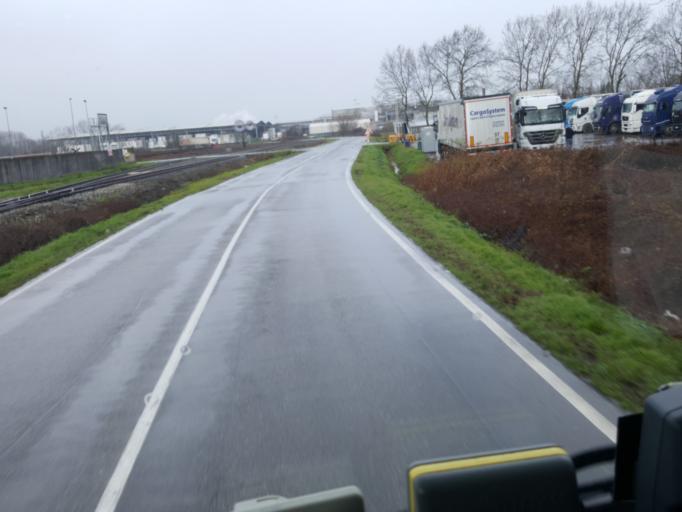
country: IT
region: Tuscany
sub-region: Provincia di Lucca
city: Porcari
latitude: 43.8258
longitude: 10.6077
